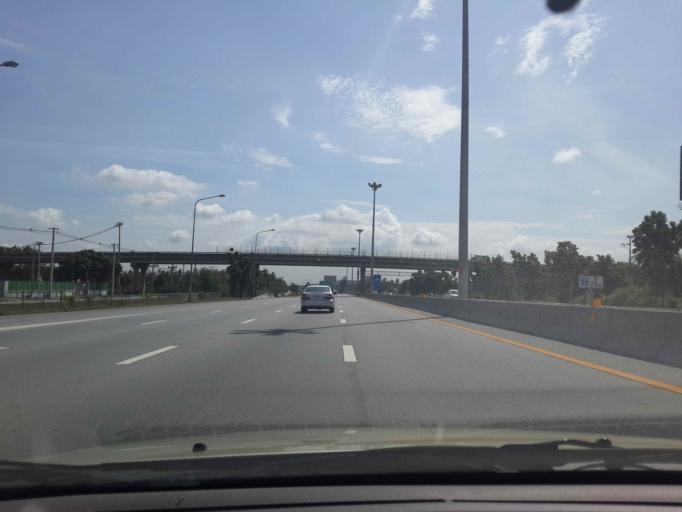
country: TH
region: Chon Buri
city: Chon Buri
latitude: 13.3228
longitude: 101.0137
